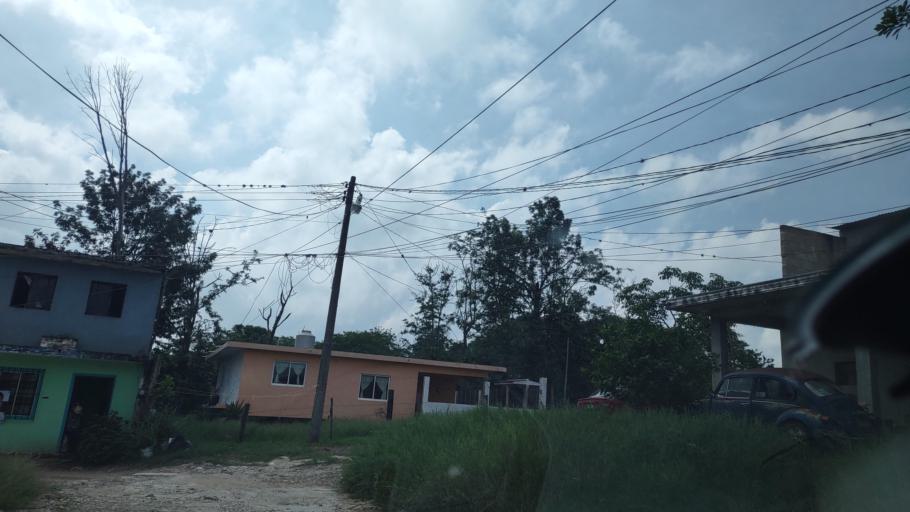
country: MX
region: Veracruz
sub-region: Emiliano Zapata
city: Jacarandas
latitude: 19.4698
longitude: -96.8354
